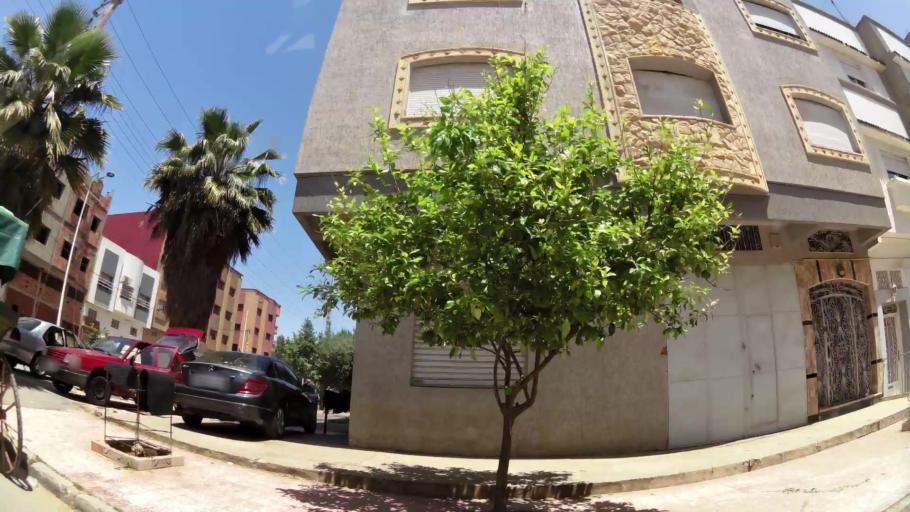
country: MA
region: Rabat-Sale-Zemmour-Zaer
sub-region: Khemisset
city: Khemisset
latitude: 33.8285
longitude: -6.0774
